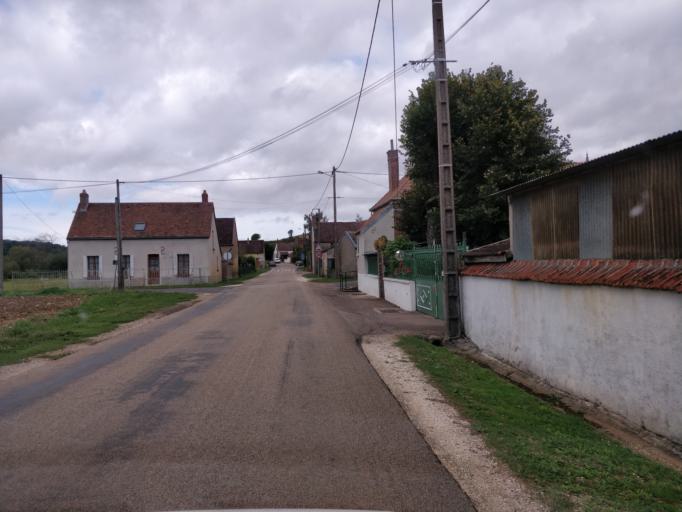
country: FR
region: Champagne-Ardenne
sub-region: Departement de l'Aube
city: Aix-en-Othe
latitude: 48.1672
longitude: 3.6281
